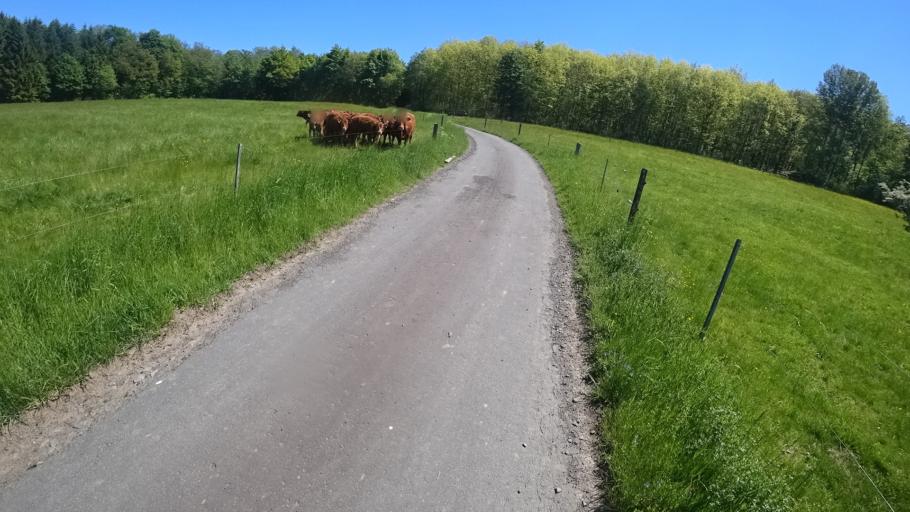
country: DE
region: Rheinland-Pfalz
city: Kausen
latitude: 50.7451
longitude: 7.8749
